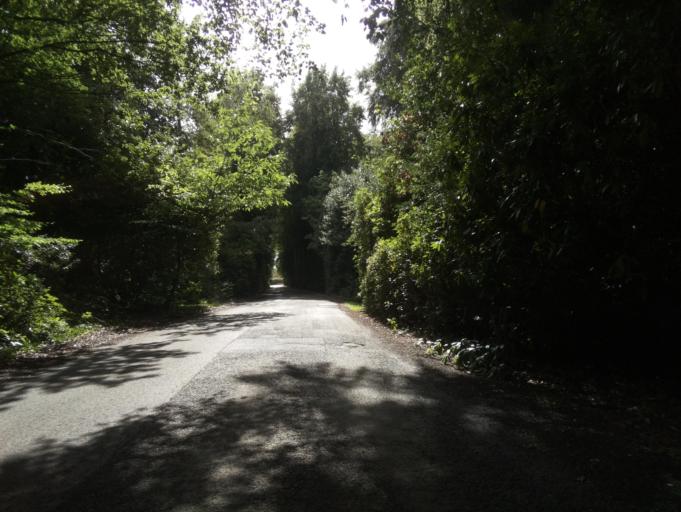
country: GB
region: England
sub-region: Staffordshire
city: Barlaston
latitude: 52.9484
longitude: -2.1574
